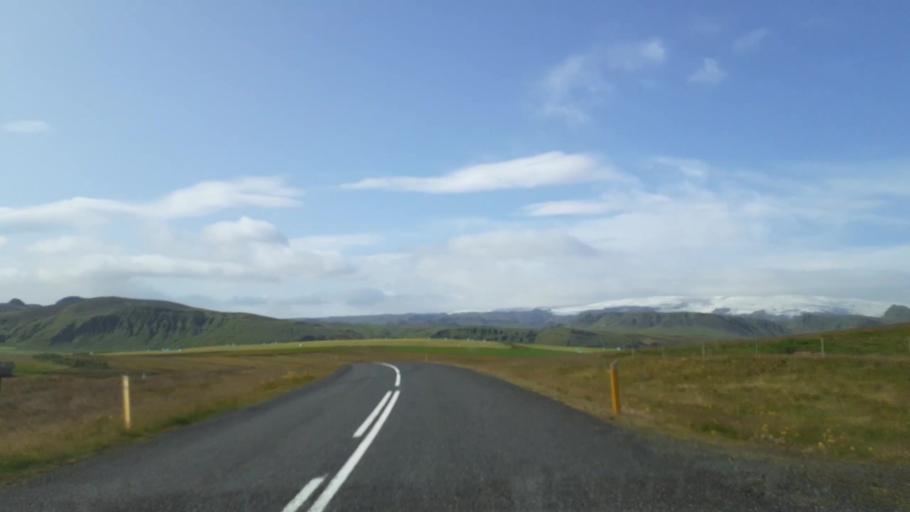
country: IS
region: South
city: Vestmannaeyjar
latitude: 63.4347
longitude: -19.0560
